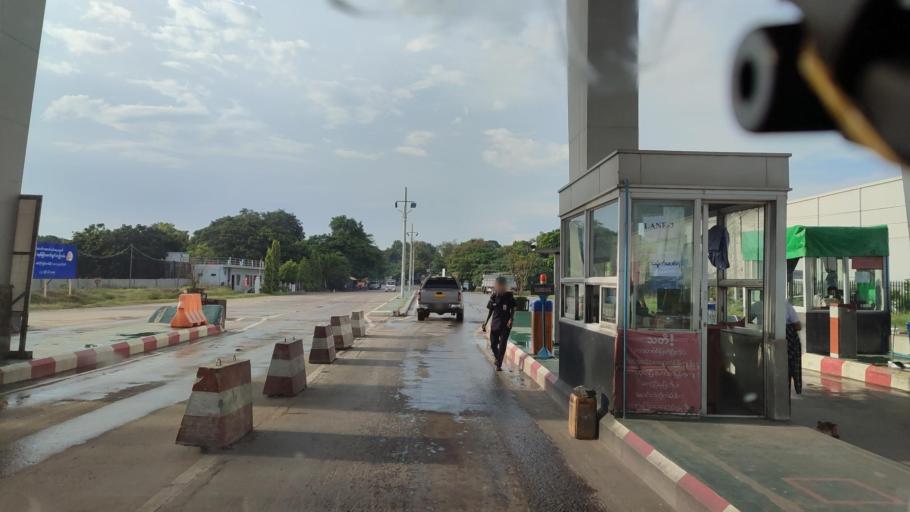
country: MM
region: Sagain
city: Sagaing
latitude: 21.8472
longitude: 96.0677
